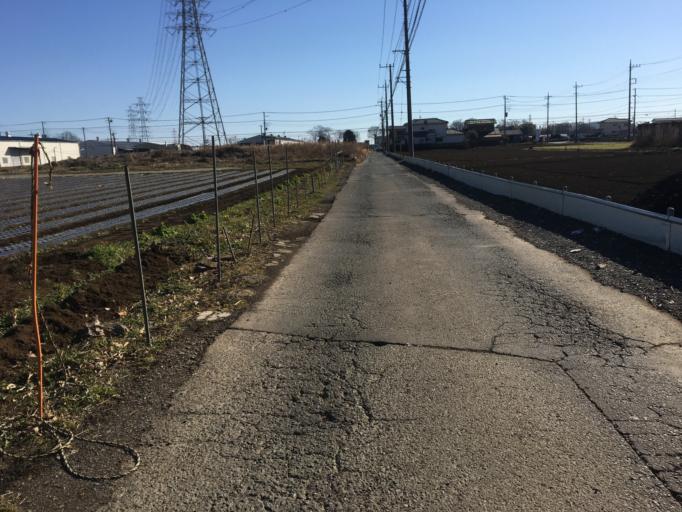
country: JP
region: Saitama
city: Oi
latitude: 35.8204
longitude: 139.5313
